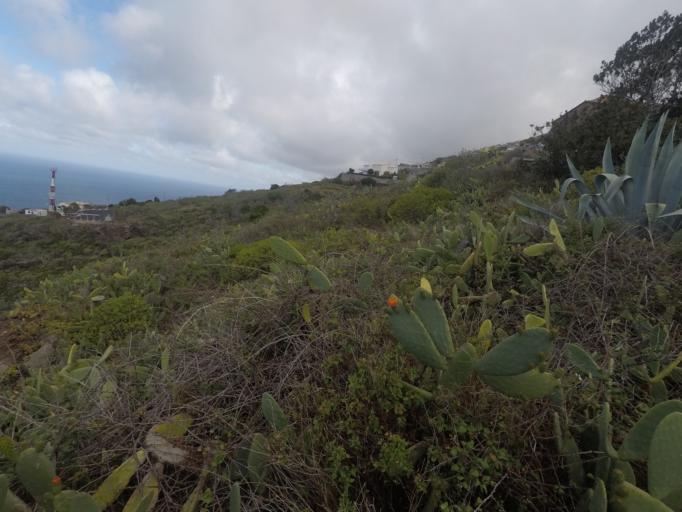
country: PT
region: Madeira
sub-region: Calheta
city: Faja da Ovelha
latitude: 32.7697
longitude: -17.2366
